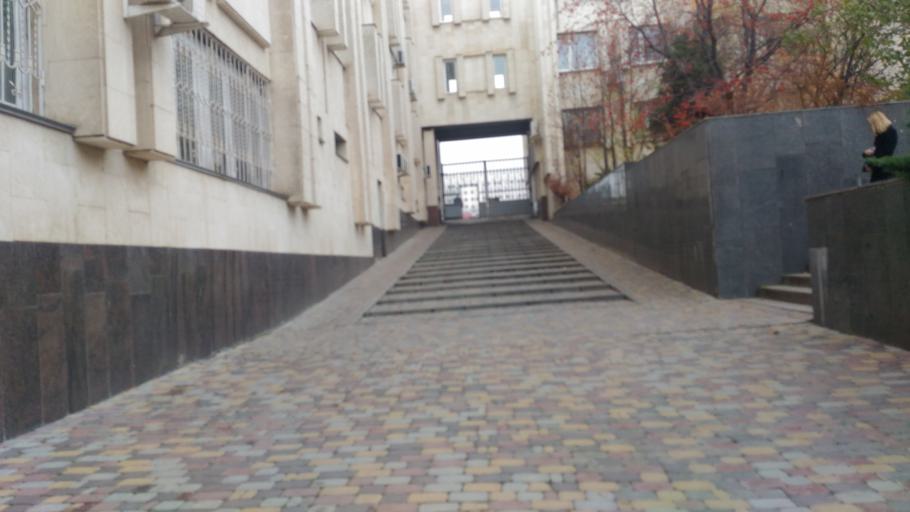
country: RU
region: Volgograd
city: Volgograd
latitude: 48.6416
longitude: 44.4224
